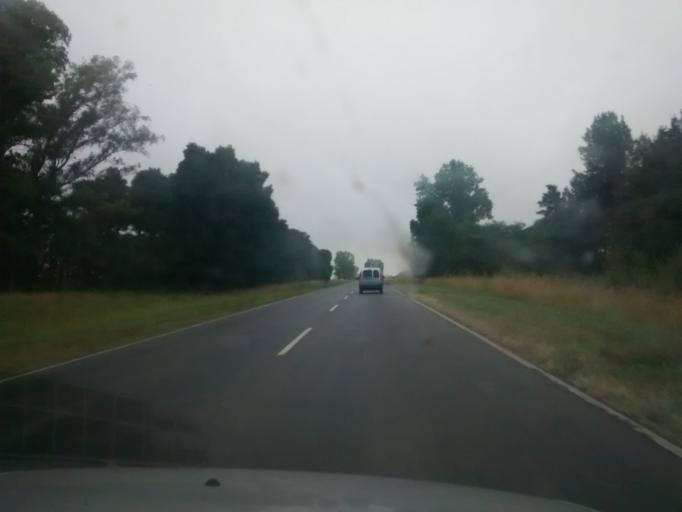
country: AR
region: Buenos Aires
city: Ranchos
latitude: -35.4422
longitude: -58.3143
